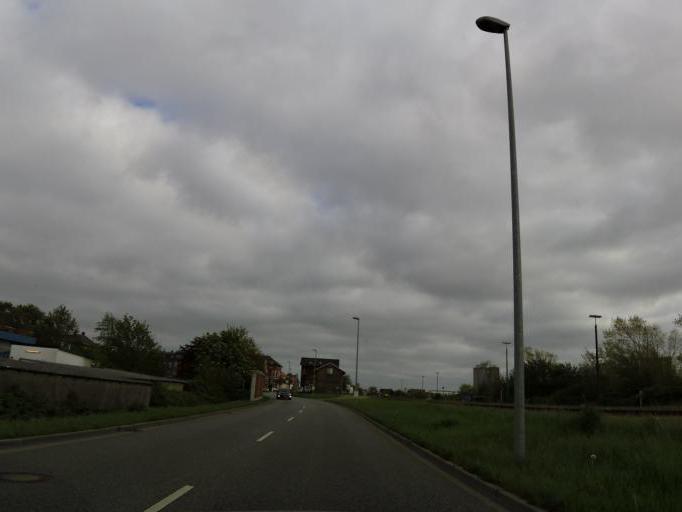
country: DE
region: Schleswig-Holstein
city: Husum
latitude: 54.4788
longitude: 9.0411
